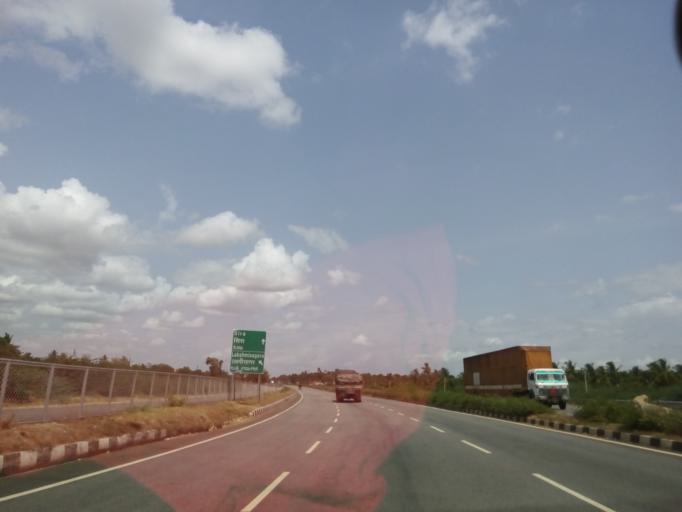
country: IN
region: Karnataka
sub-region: Tumkur
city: Sira
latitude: 13.7933
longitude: 76.8057
